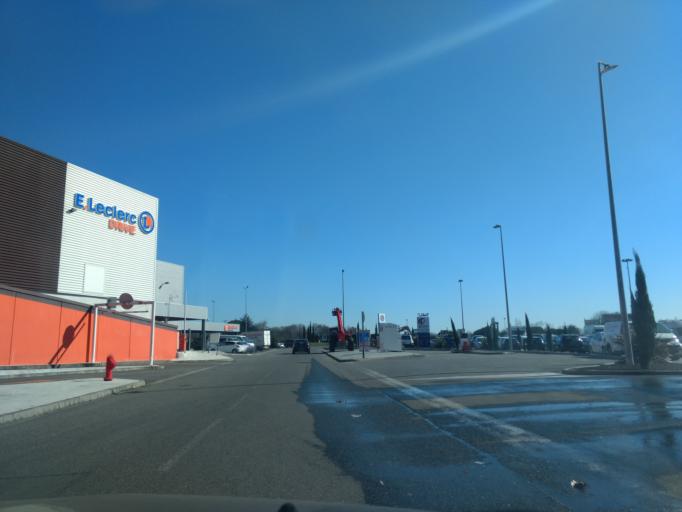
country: FR
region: Midi-Pyrenees
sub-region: Departement de la Haute-Garonne
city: Roquettes
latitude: 43.5126
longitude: 1.3683
